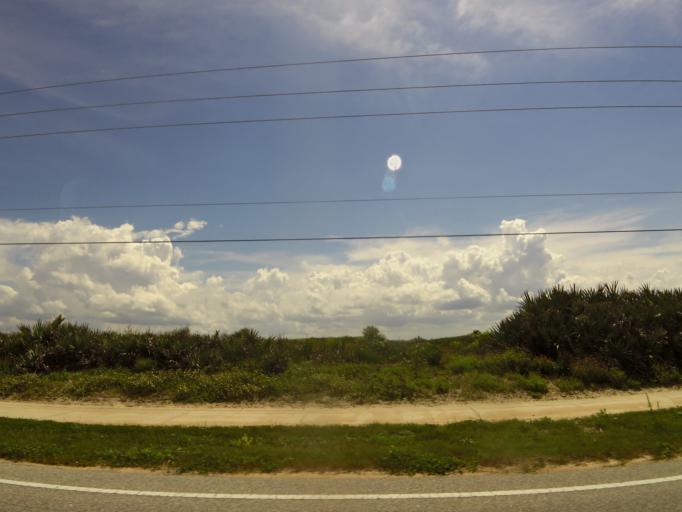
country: US
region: Florida
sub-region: Volusia County
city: Ormond-by-the-Sea
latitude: 29.3980
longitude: -81.0893
